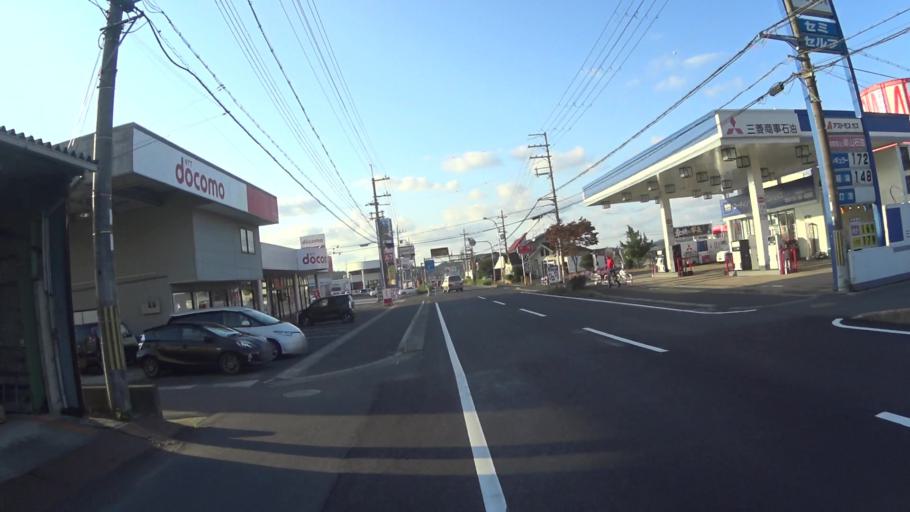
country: JP
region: Kyoto
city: Miyazu
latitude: 35.6065
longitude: 135.0819
